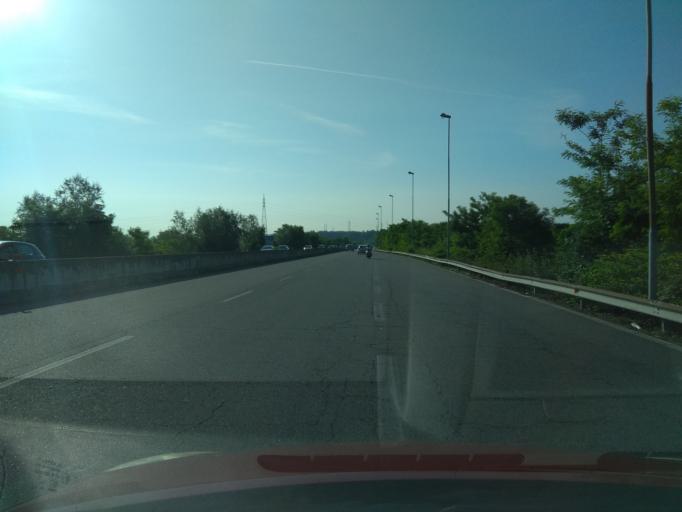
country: IT
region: Piedmont
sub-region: Provincia di Biella
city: Gaglianico
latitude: 45.5593
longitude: 8.0796
